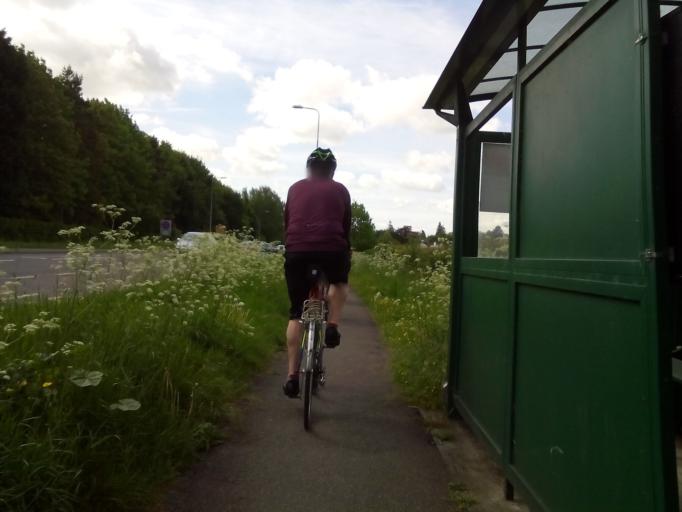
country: GB
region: England
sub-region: Cambridgeshire
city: Harston
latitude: 52.1485
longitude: 0.0910
